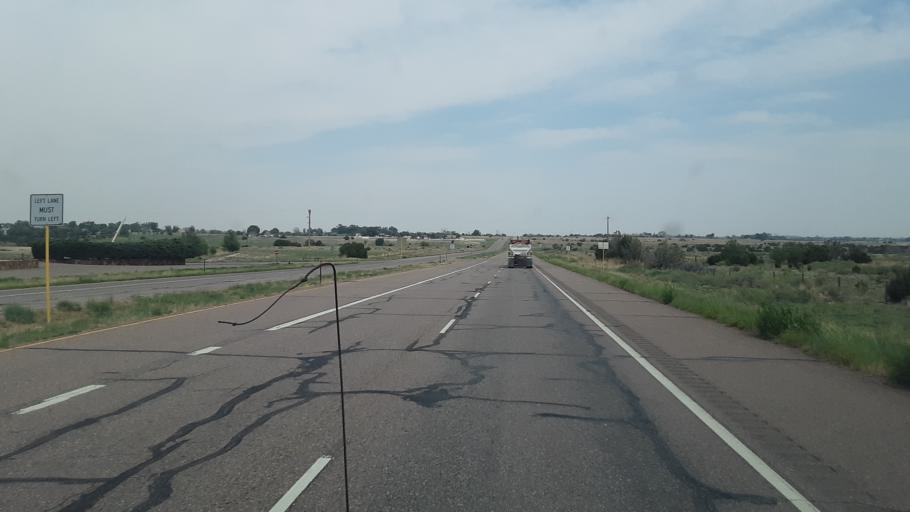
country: US
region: Colorado
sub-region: Fremont County
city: Penrose
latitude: 38.4120
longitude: -105.0164
